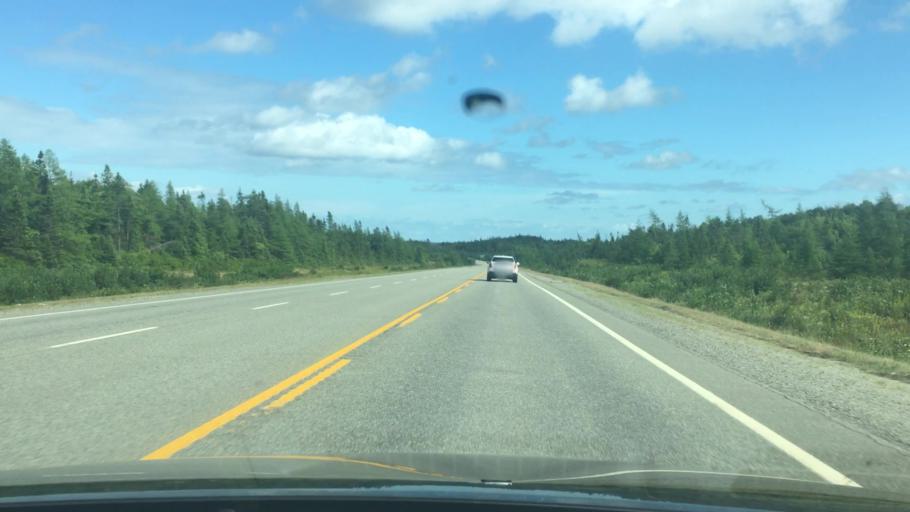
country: CA
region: Nova Scotia
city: Port Hawkesbury
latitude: 45.6179
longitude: -61.1063
